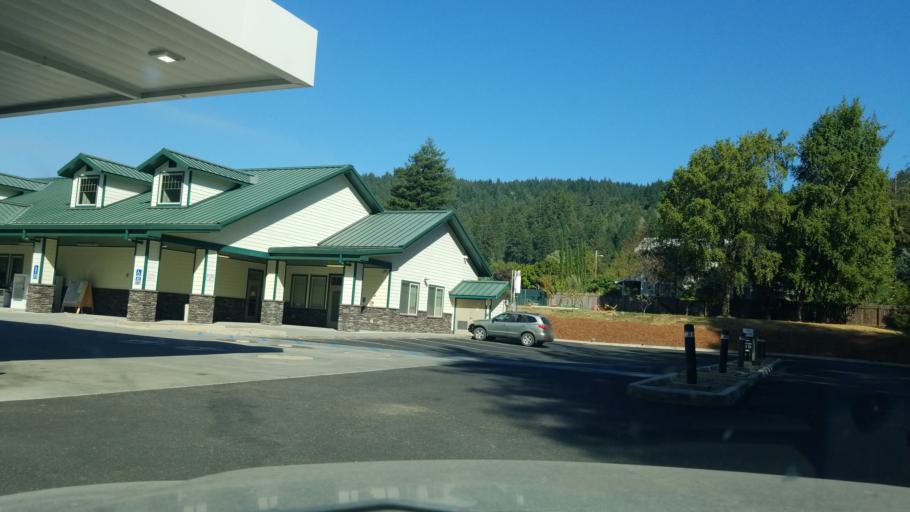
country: US
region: California
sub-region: Humboldt County
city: Redway
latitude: 40.2346
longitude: -123.8241
